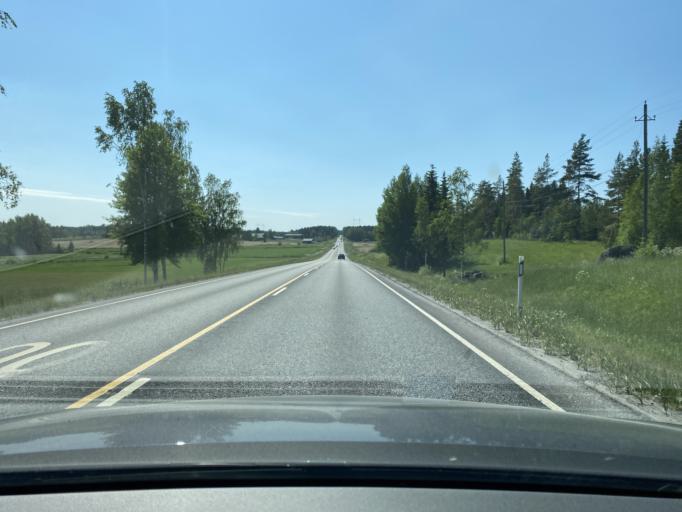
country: FI
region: Pirkanmaa
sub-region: Tampere
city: Nokia
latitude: 61.4199
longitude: 23.3289
